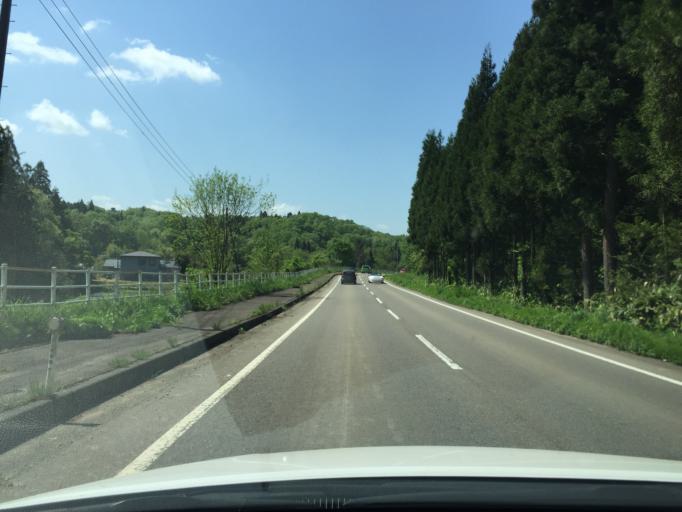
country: JP
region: Niigata
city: Kamo
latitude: 37.5790
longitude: 139.0931
